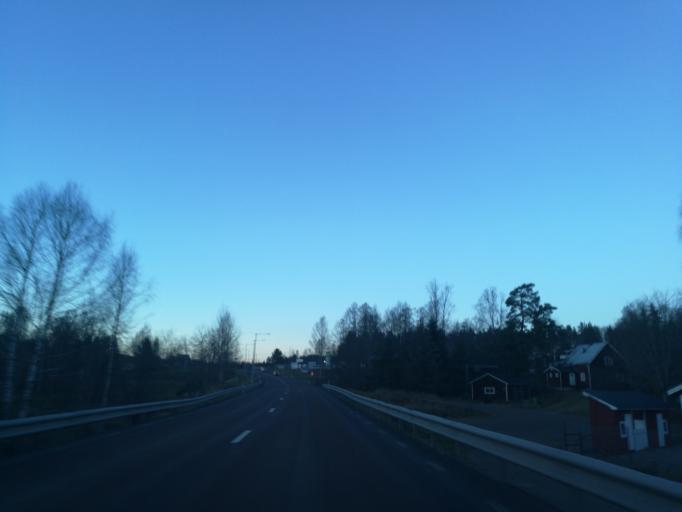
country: SE
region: Vaermland
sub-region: Eda Kommun
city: Charlottenberg
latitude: 59.9184
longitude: 12.2725
